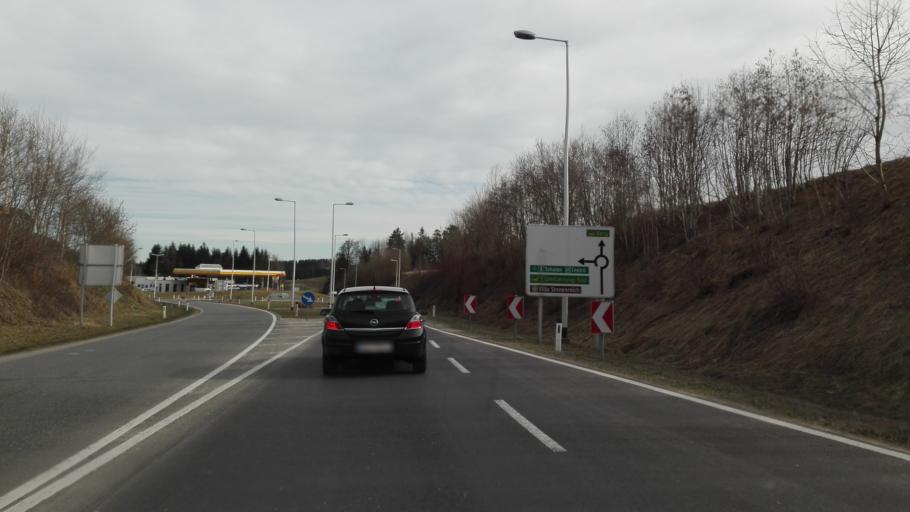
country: AT
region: Upper Austria
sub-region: Politischer Bezirk Rohrbach
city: Schlaegl
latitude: 48.5667
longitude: 13.9835
